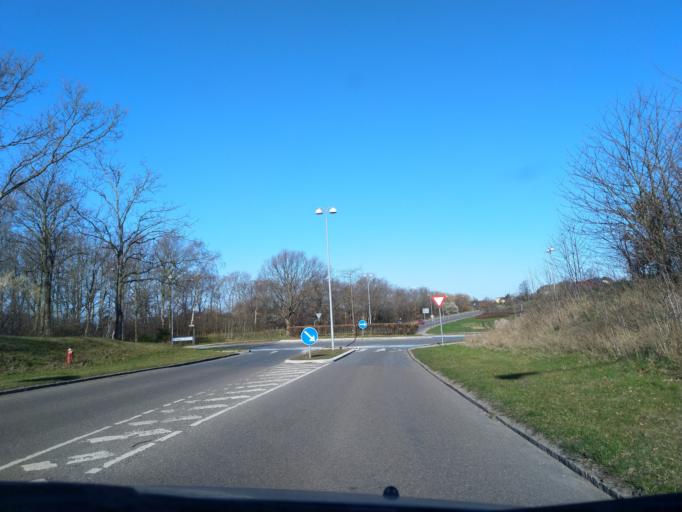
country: DK
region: Zealand
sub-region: Kalundborg Kommune
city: Kalundborg
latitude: 55.6880
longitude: 11.0578
